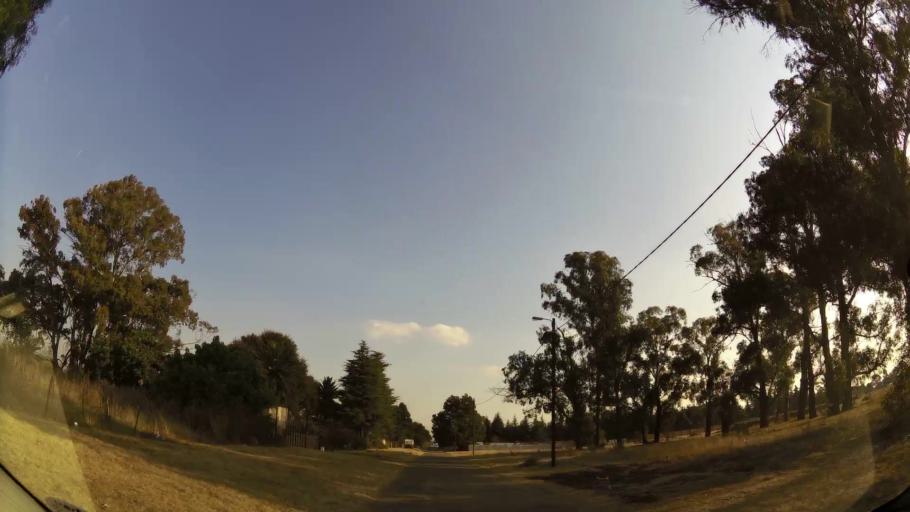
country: ZA
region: Gauteng
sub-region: Ekurhuleni Metropolitan Municipality
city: Benoni
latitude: -26.1476
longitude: 28.3738
